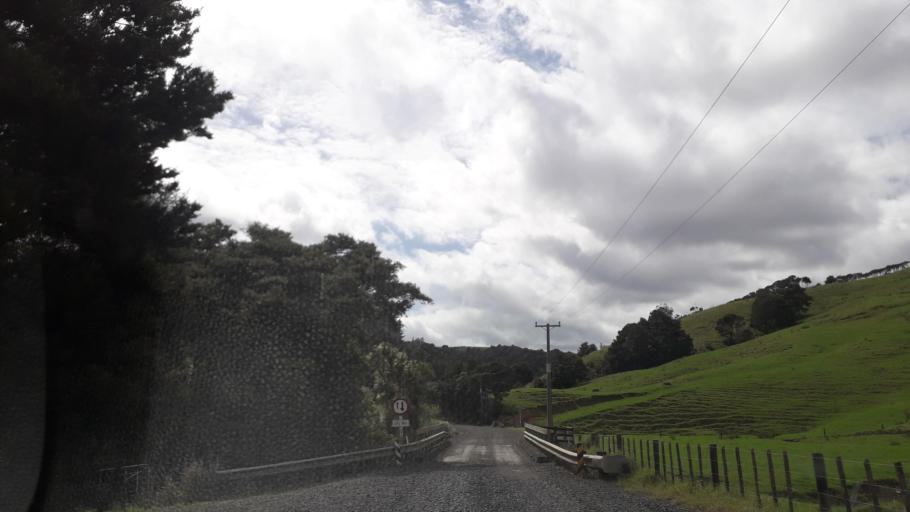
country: NZ
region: Northland
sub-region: Far North District
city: Ahipara
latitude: -35.2388
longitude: 173.2630
